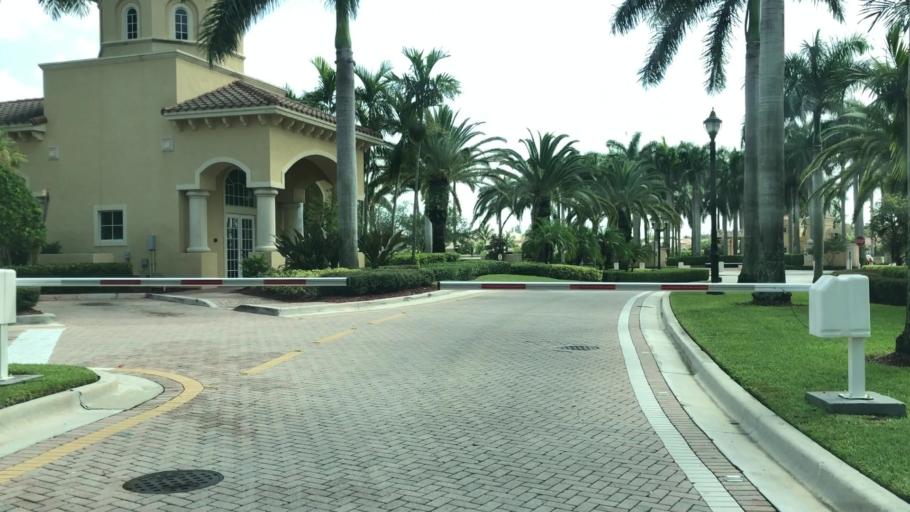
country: US
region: Florida
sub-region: Miami-Dade County
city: Palm Springs North
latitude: 25.9647
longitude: -80.3761
